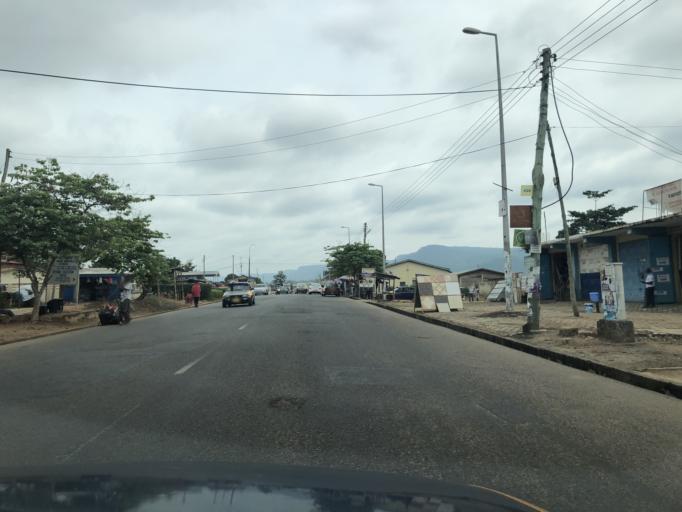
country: GH
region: Eastern
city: Koforidua
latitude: 6.1036
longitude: -0.2668
